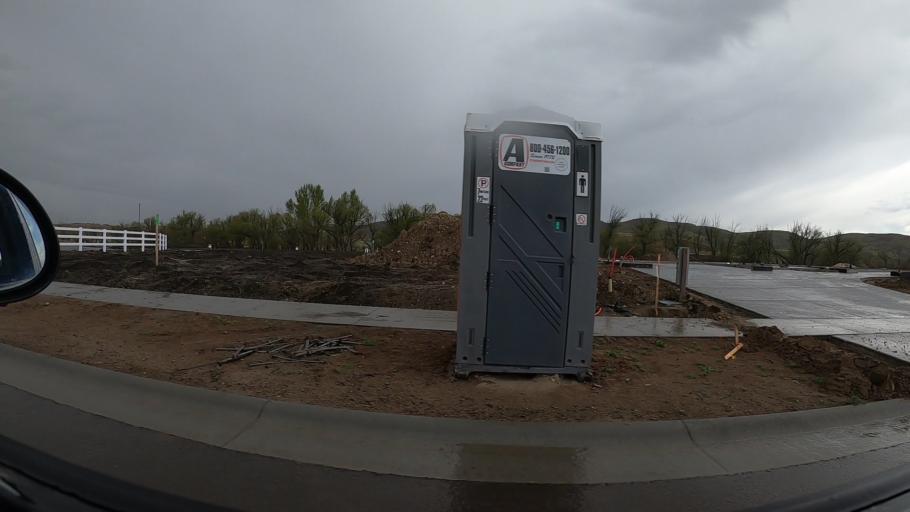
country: US
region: Idaho
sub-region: Ada County
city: Eagle
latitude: 43.7327
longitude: -116.2845
